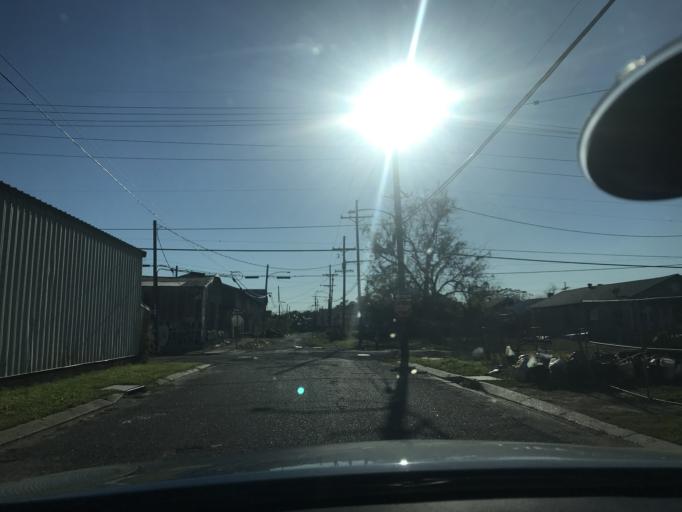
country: US
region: Louisiana
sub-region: Orleans Parish
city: New Orleans
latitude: 29.9538
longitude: -90.0994
